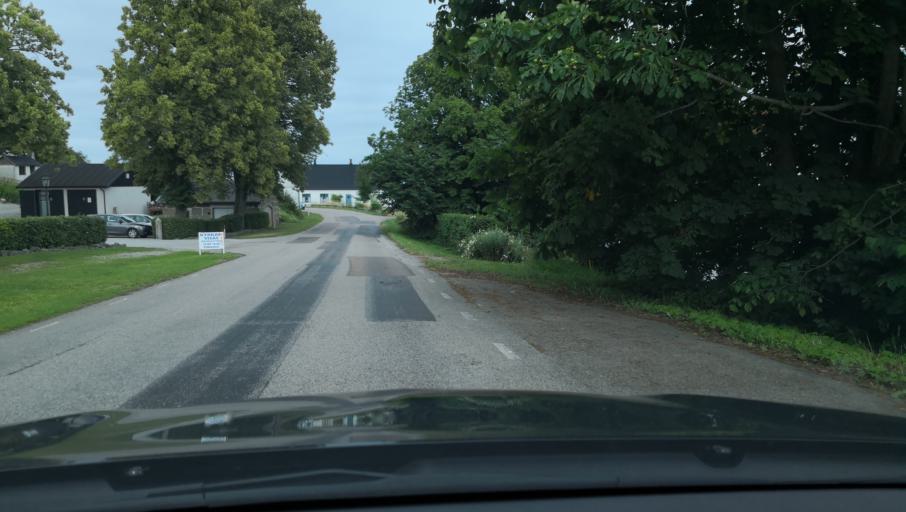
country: SE
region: Skane
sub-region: Simrishamns Kommun
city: Kivik
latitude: 55.6939
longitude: 14.1686
